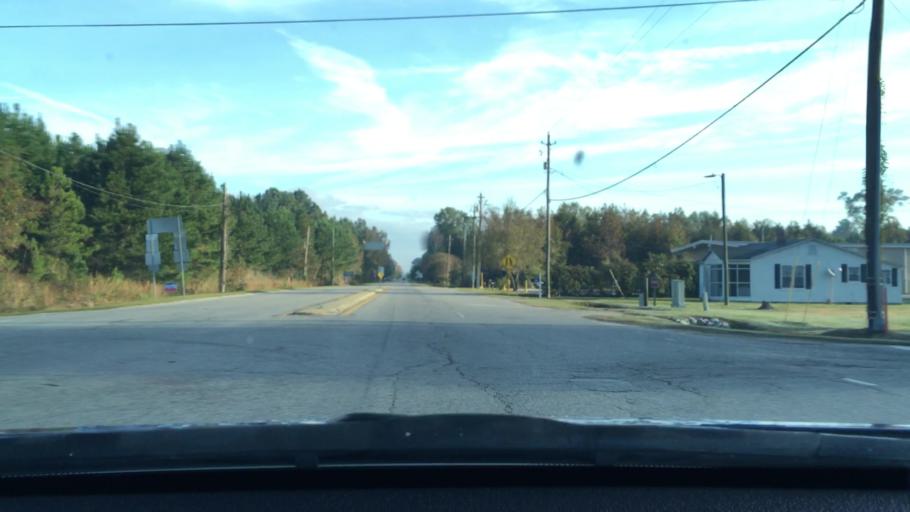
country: US
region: South Carolina
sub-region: Sumter County
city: East Sumter
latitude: 33.9374
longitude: -80.3193
